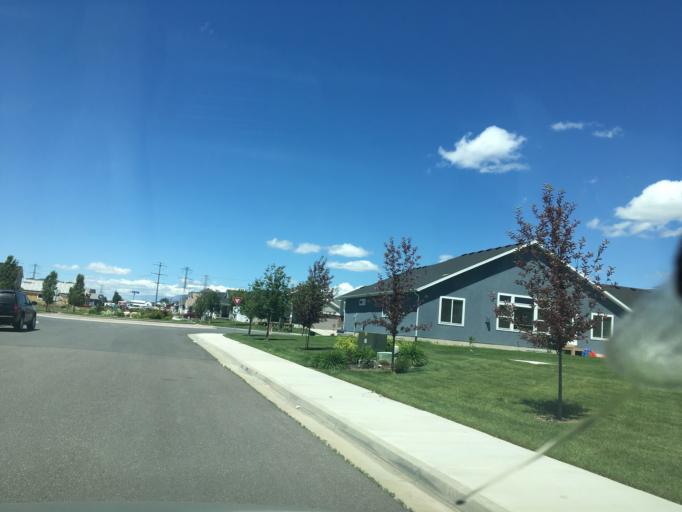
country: US
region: Utah
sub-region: Davis County
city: Layton
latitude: 41.0527
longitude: -112.0089
